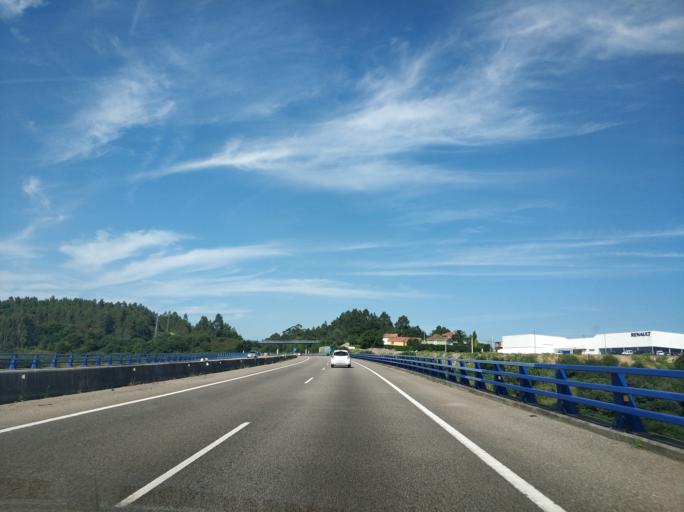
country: ES
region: Asturias
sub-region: Province of Asturias
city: Soto del Barco
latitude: 43.5321
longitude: -6.0493
